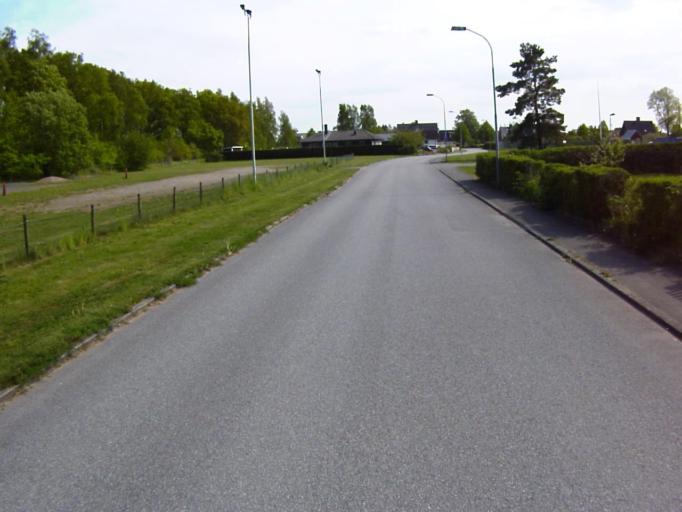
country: SE
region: Skane
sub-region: Kristianstads Kommun
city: Kristianstad
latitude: 56.0573
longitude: 14.0884
